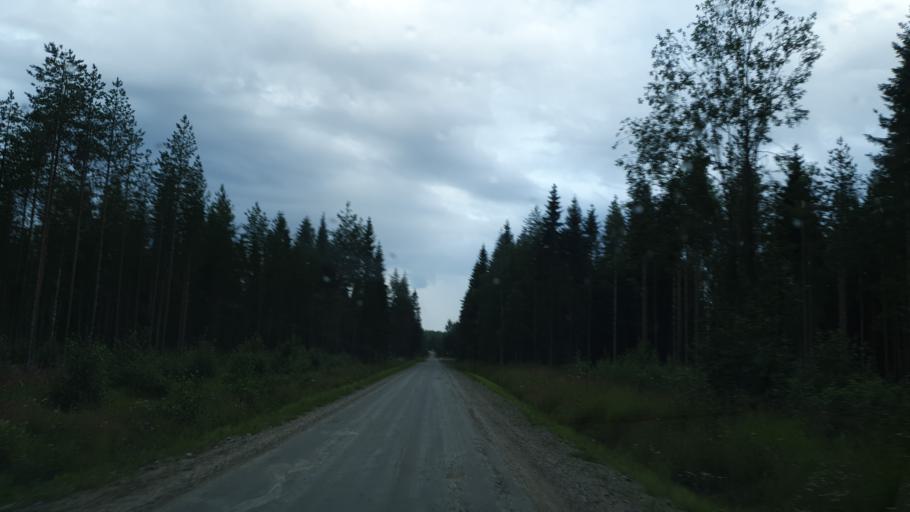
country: FI
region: Kainuu
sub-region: Kehys-Kainuu
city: Kuhmo
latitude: 64.2140
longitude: 29.3686
